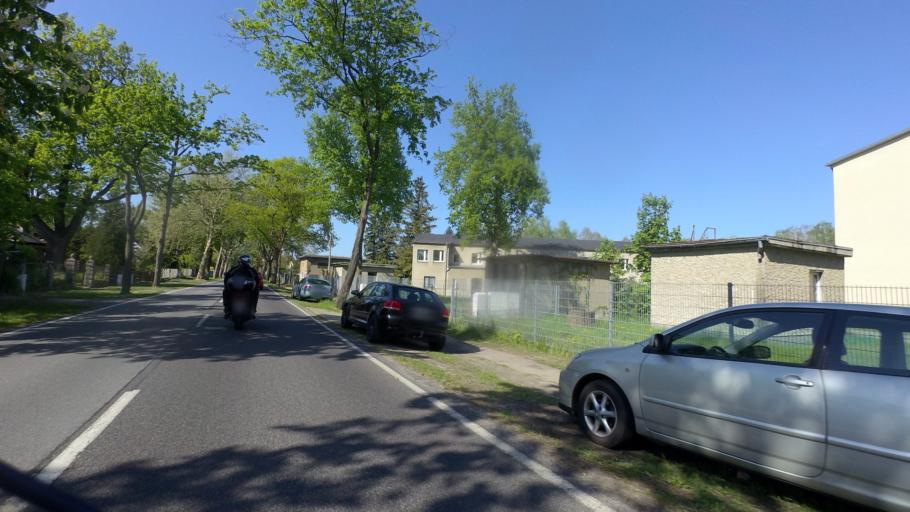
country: DE
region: Brandenburg
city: Bestensee
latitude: 52.2340
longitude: 13.6677
